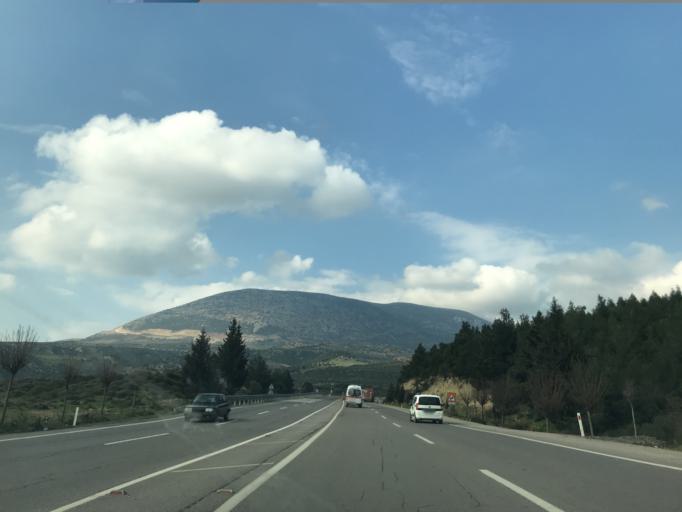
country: TR
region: Hatay
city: Belen
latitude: 36.4562
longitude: 36.2718
